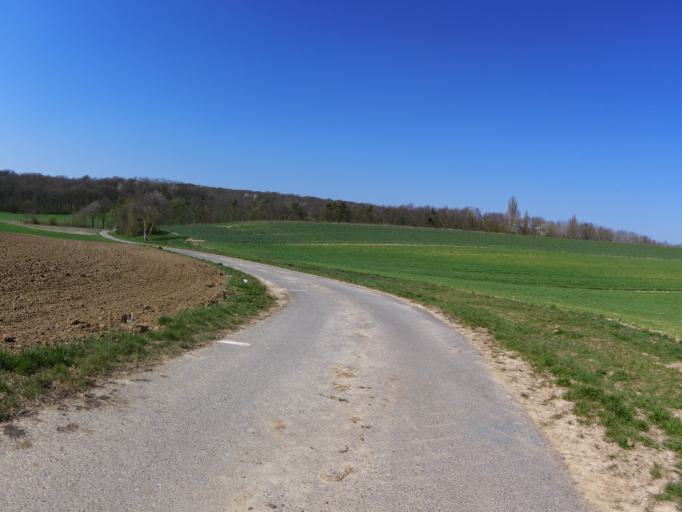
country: DE
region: Bavaria
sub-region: Regierungsbezirk Unterfranken
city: Rottendorf
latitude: 49.8204
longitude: 10.0733
